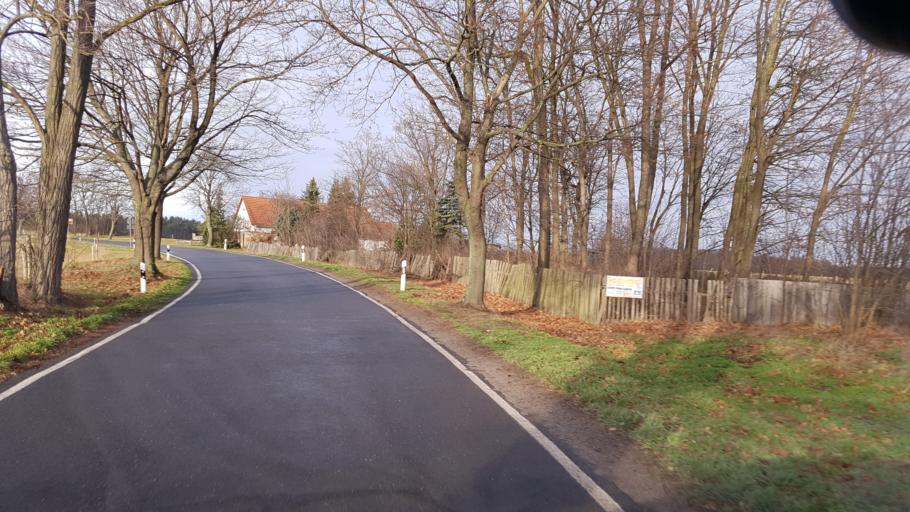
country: DE
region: Brandenburg
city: Altdobern
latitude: 51.6654
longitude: 13.9935
